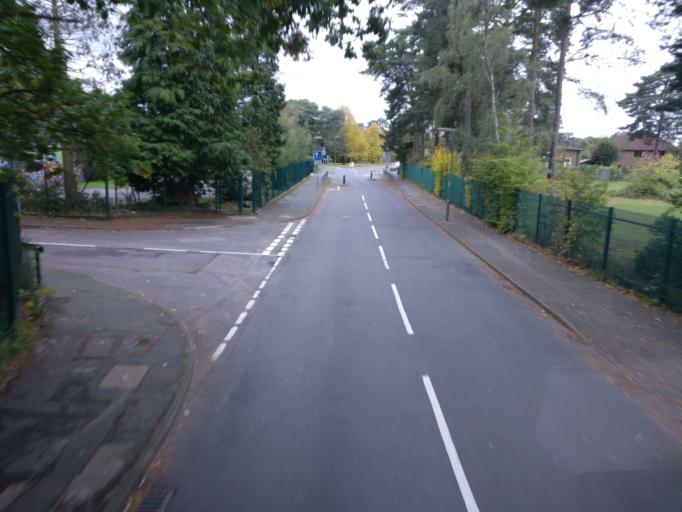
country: GB
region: England
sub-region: Surrey
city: Camberley
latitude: 51.3494
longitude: -0.7229
